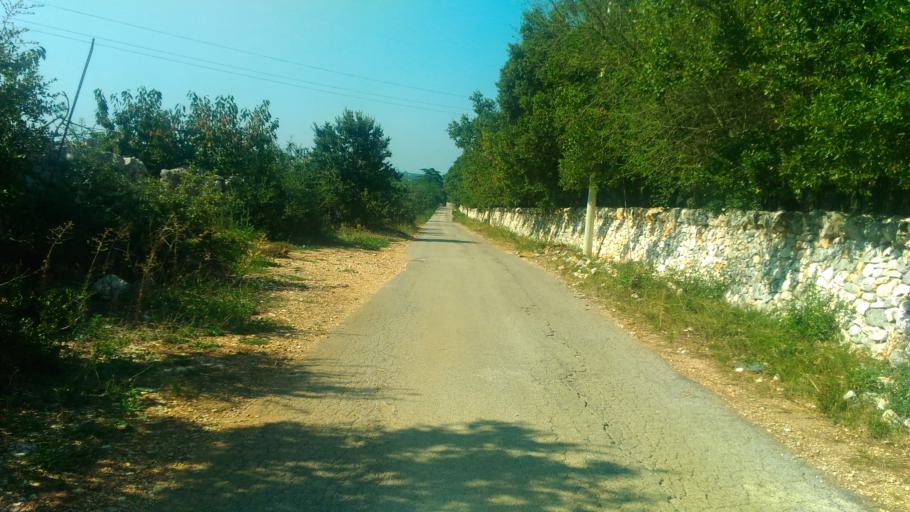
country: IT
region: Apulia
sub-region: Provincia di Bari
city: Noci
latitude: 40.8169
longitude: 17.1775
